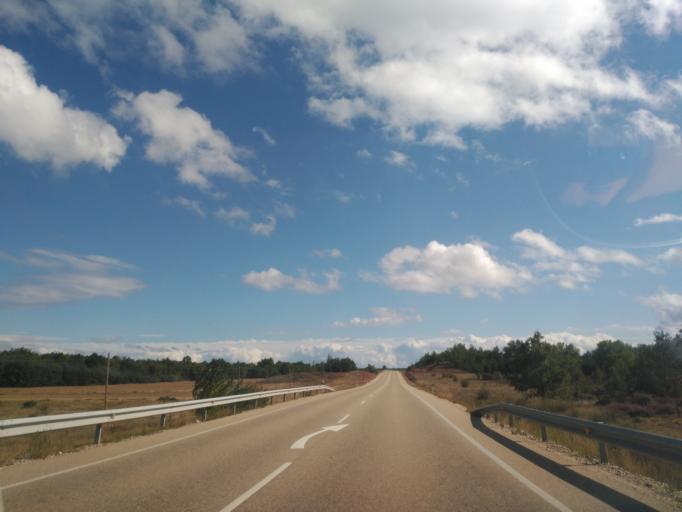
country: ES
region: Castille and Leon
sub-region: Provincia de Burgos
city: Hacinas
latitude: 41.9656
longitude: -3.2939
